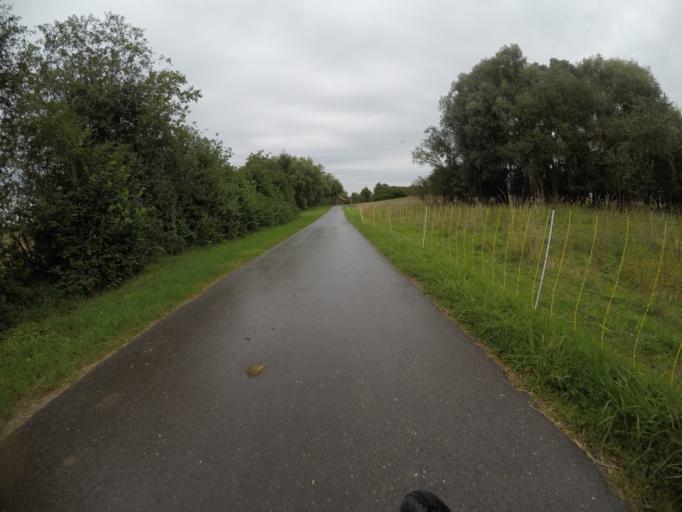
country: DE
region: Baden-Wuerttemberg
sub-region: Regierungsbezirk Stuttgart
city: Nufringen
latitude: 48.6239
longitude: 8.9077
